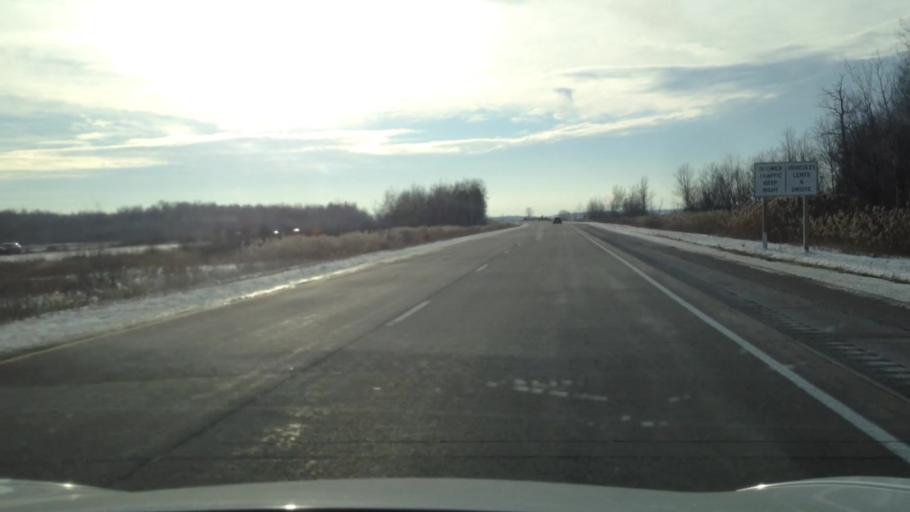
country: CA
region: Ontario
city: Hawkesbury
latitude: 45.4314
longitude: -74.7505
